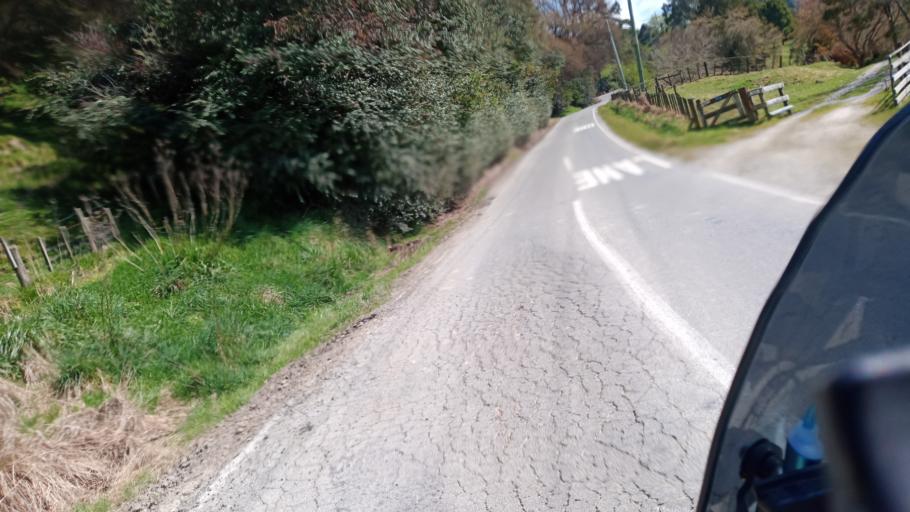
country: NZ
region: Gisborne
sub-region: Gisborne District
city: Gisborne
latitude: -38.7875
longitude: 177.7925
